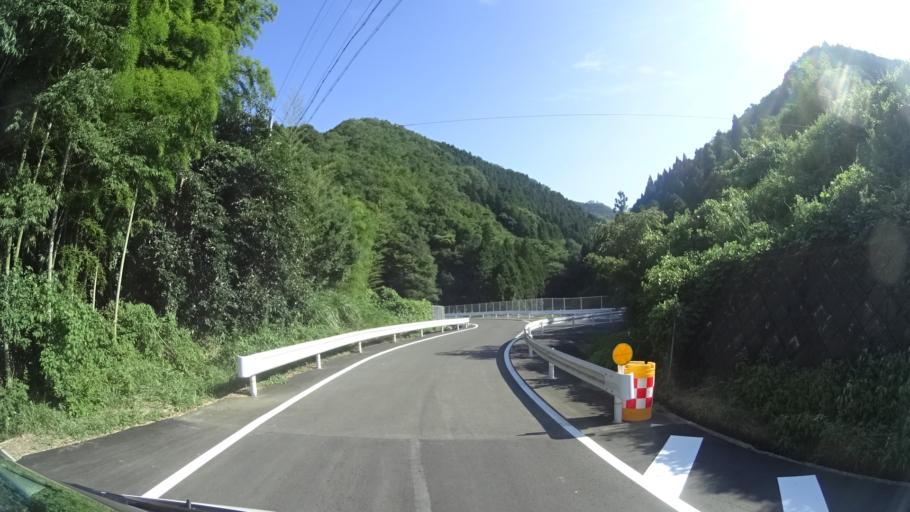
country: JP
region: Kyoto
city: Ayabe
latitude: 35.2699
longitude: 135.3618
